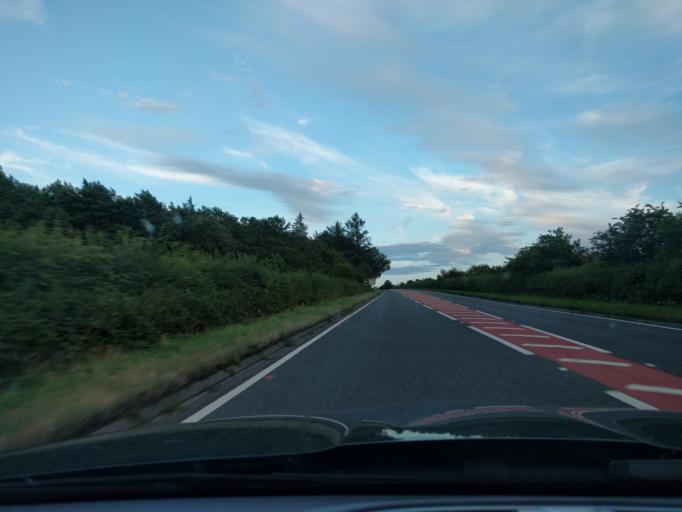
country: GB
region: England
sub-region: Northumberland
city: Felton
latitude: 55.2631
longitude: -1.7104
